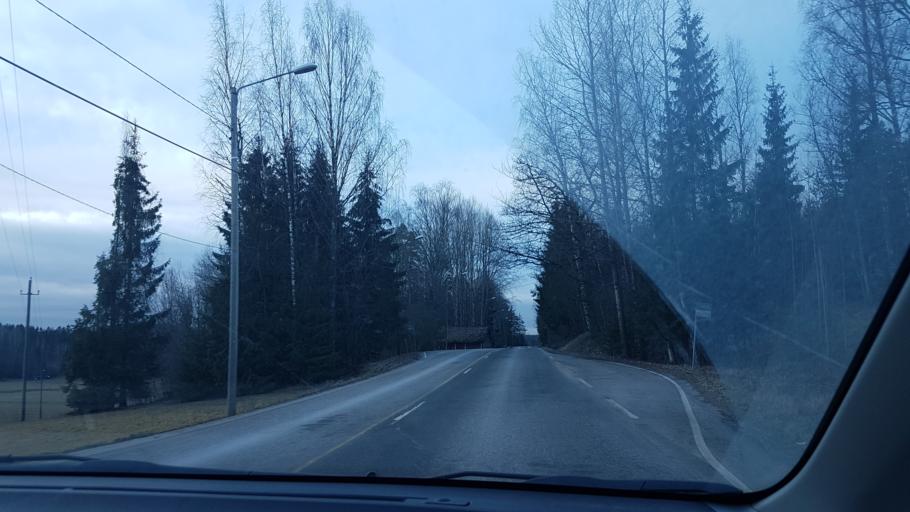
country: FI
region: Uusimaa
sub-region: Helsinki
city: Nurmijaervi
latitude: 60.3549
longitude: 24.7450
